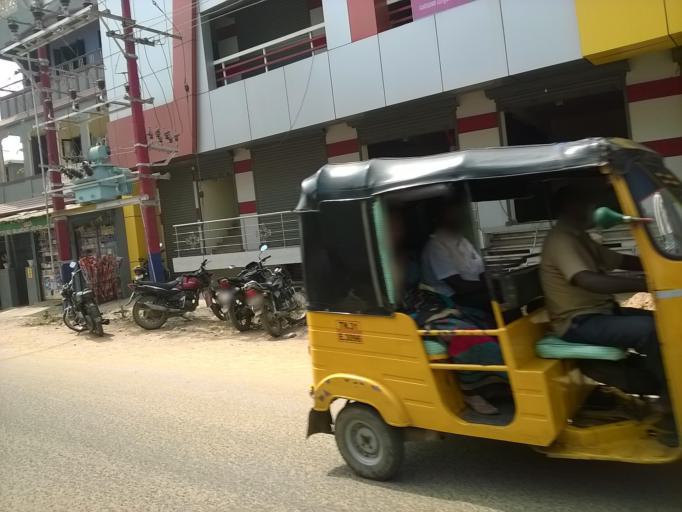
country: IN
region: Tamil Nadu
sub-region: Cuddalore
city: Panruti
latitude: 11.7693
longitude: 79.5529
